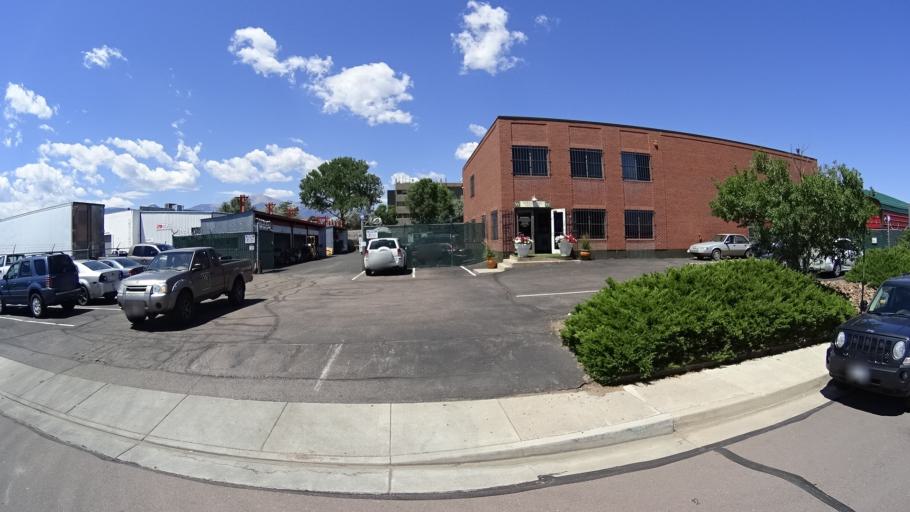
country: US
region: Colorado
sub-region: El Paso County
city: Colorado Springs
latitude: 38.8962
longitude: -104.8255
